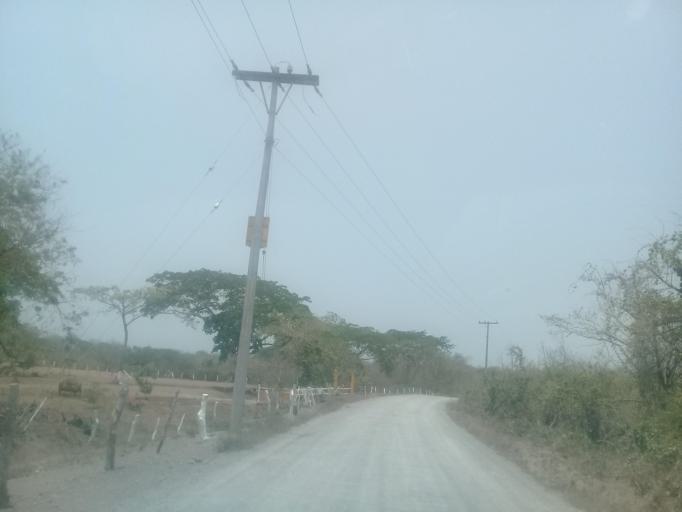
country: MX
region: Veracruz
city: Jamapa
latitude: 19.0875
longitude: -96.2362
